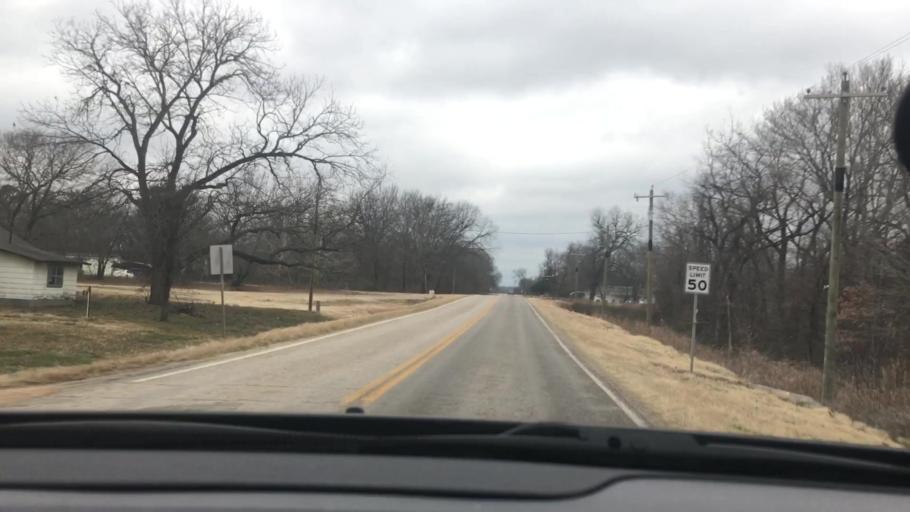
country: US
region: Oklahoma
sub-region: Coal County
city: Coalgate
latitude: 34.3750
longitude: -96.4281
